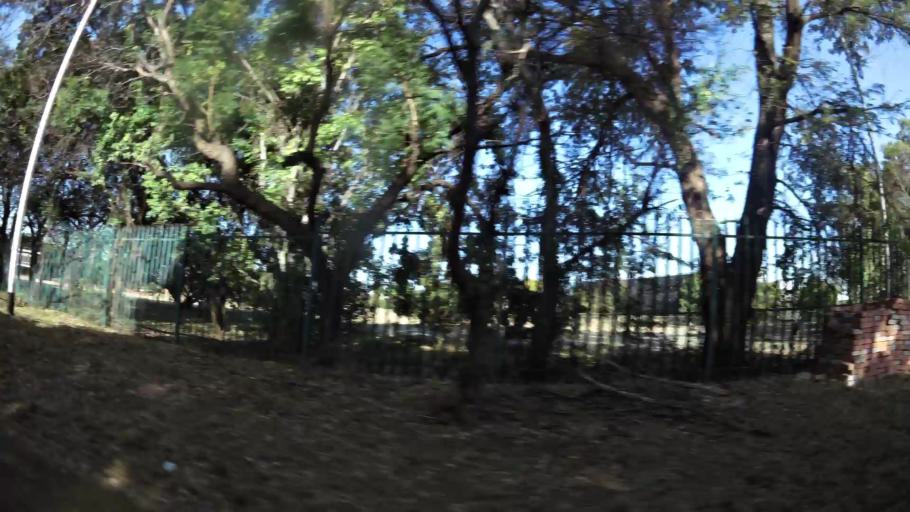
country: ZA
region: Gauteng
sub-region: City of Tshwane Metropolitan Municipality
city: Pretoria
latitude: -25.7112
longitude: 28.2575
